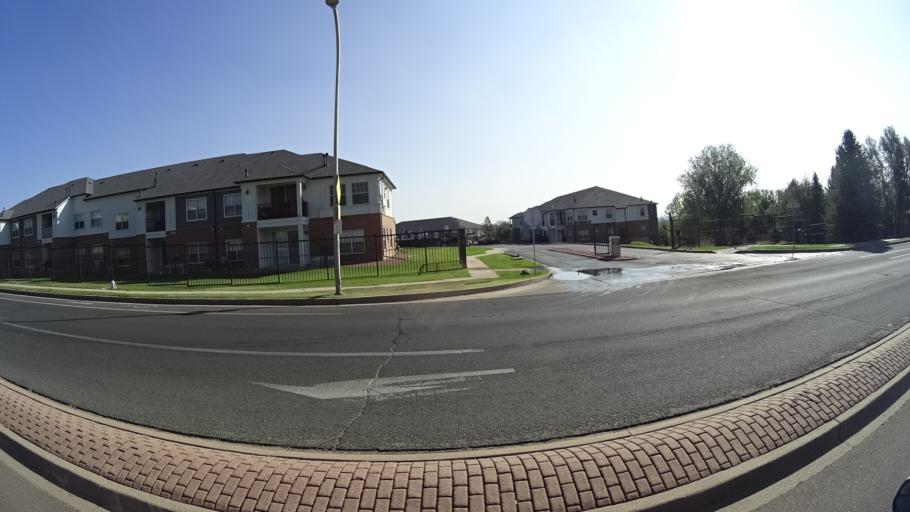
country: US
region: Colorado
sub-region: El Paso County
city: Colorado Springs
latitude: 38.8029
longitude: -104.8543
